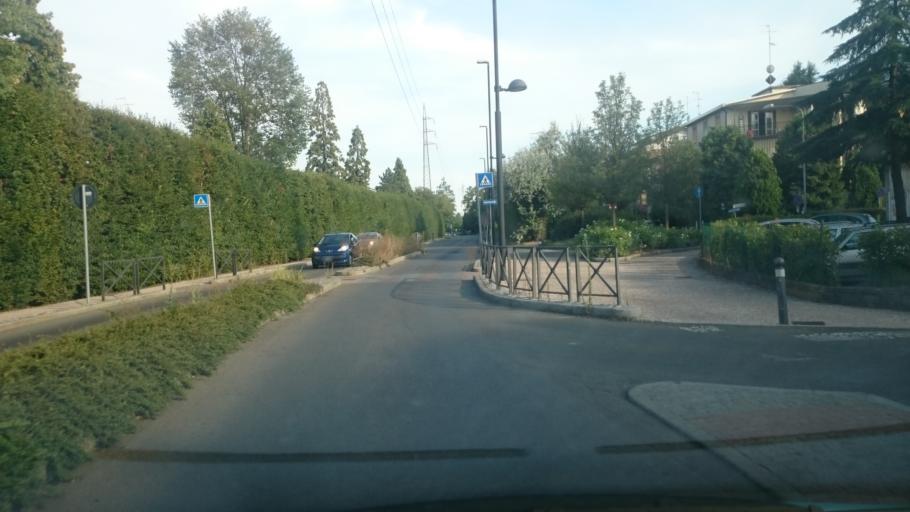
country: IT
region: Emilia-Romagna
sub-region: Provincia di Reggio Emilia
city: Reggio nell'Emilia
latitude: 44.6804
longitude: 10.6209
